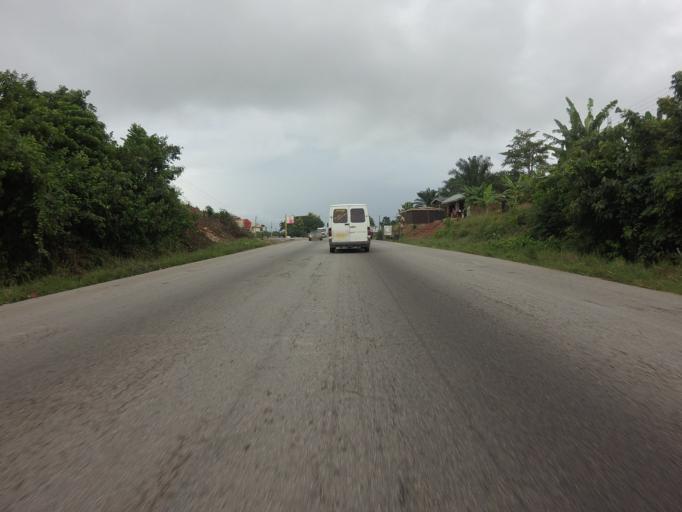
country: GH
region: Ashanti
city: Konongo
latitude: 6.6155
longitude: -1.1550
